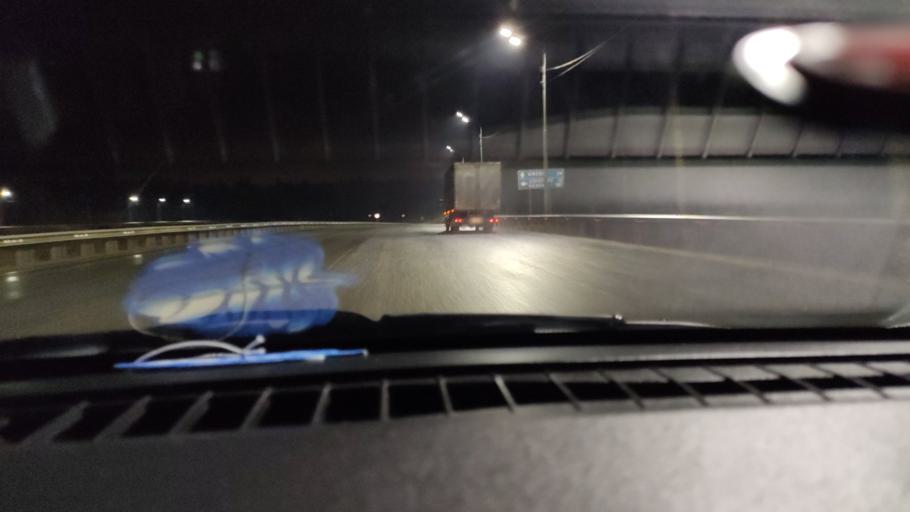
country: RU
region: Udmurtiya
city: Khokhryaki
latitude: 56.9168
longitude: 53.4525
